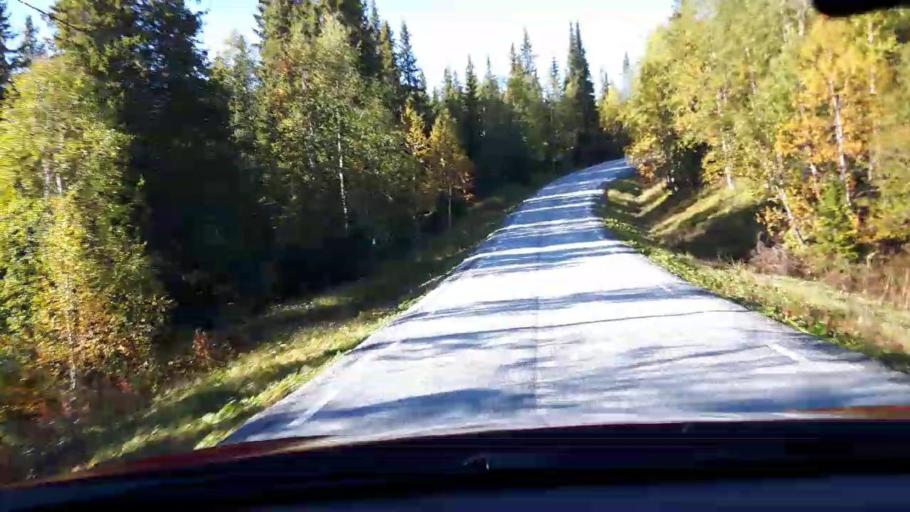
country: NO
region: Nord-Trondelag
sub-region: Royrvik
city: Royrvik
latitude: 64.8154
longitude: 14.1905
